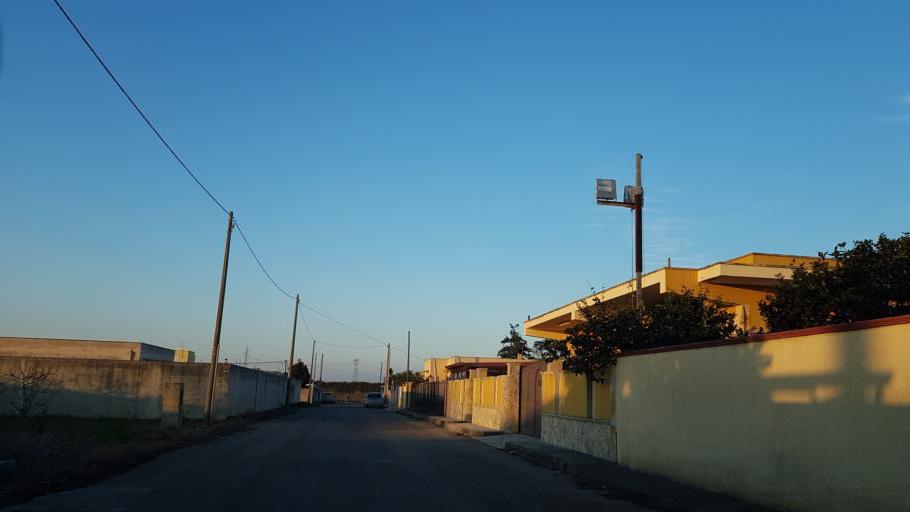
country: IT
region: Apulia
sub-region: Provincia di Brindisi
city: Tuturano
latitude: 40.5474
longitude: 17.9450
